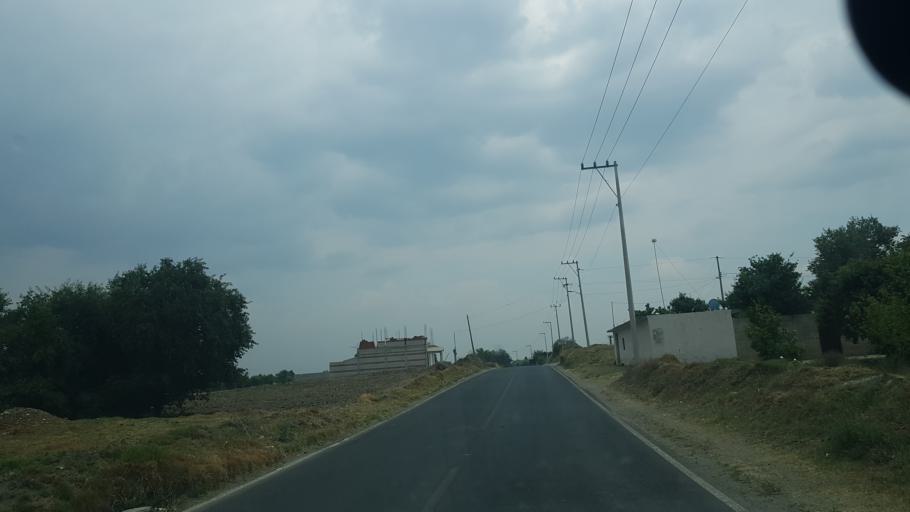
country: MX
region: Puebla
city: San Lorenzo Chiautzingo
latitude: 19.1986
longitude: -98.4533
